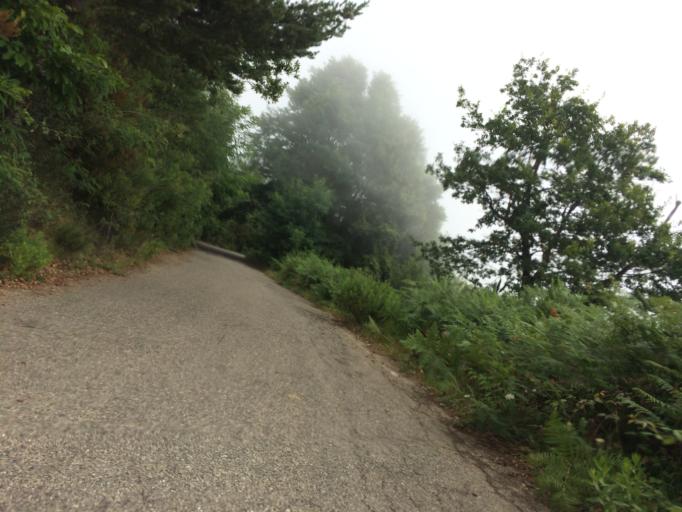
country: IT
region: Liguria
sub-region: Provincia di Imperia
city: Ceriana
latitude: 43.8564
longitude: 7.7447
